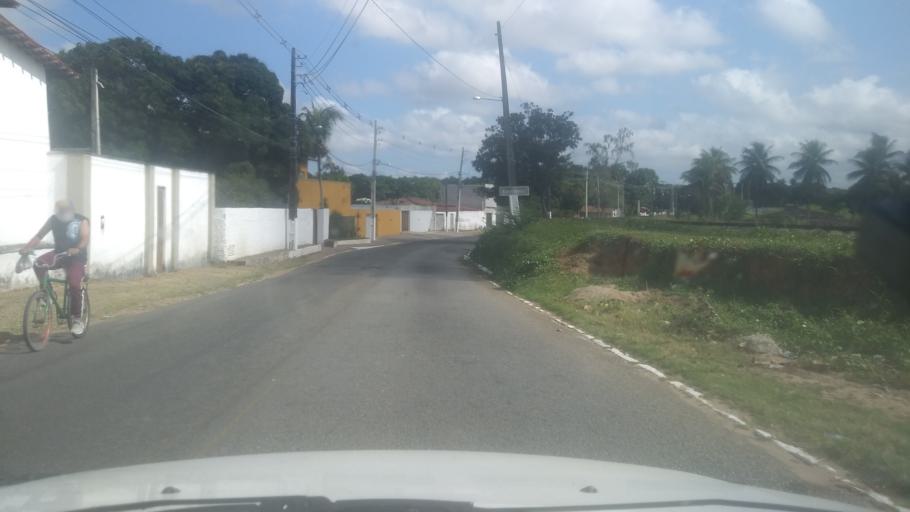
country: BR
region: Rio Grande do Norte
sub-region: Extremoz
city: Extremoz
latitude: -5.7068
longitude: -35.2808
